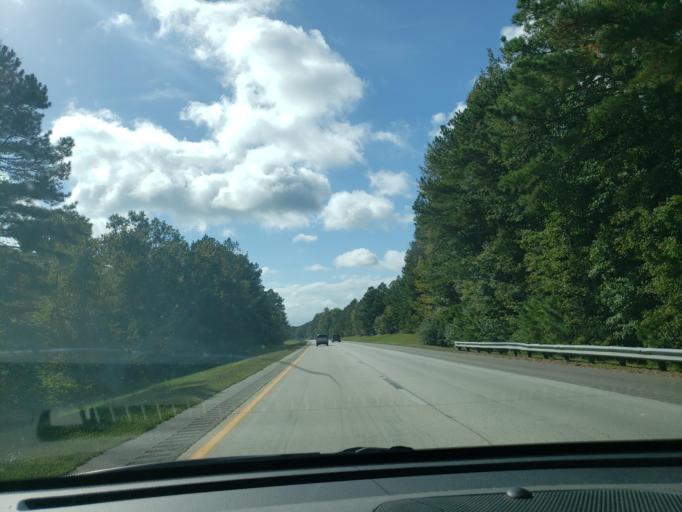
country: US
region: North Carolina
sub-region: Granville County
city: Oxford
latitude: 36.3215
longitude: -78.5224
